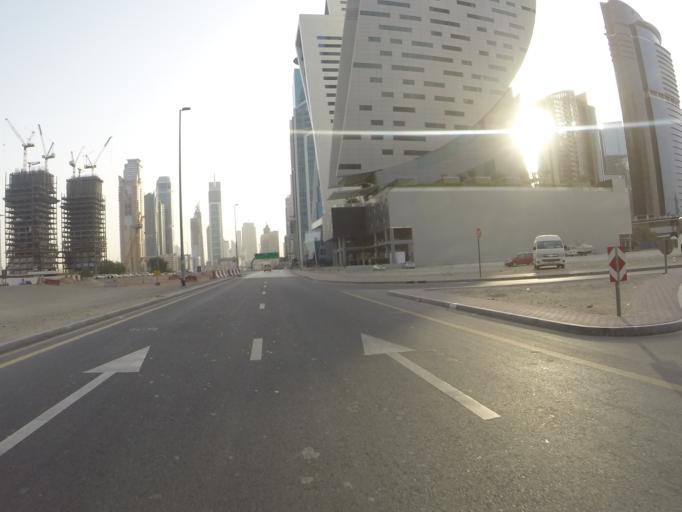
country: AE
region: Dubai
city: Dubai
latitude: 25.1853
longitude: 55.2588
